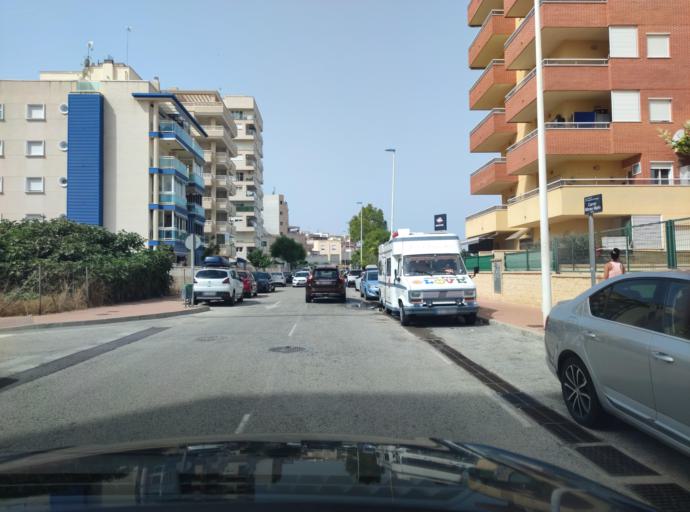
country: ES
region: Valencia
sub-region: Provincia de Alicante
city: Guardamar del Segura
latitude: 38.0965
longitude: -0.6563
